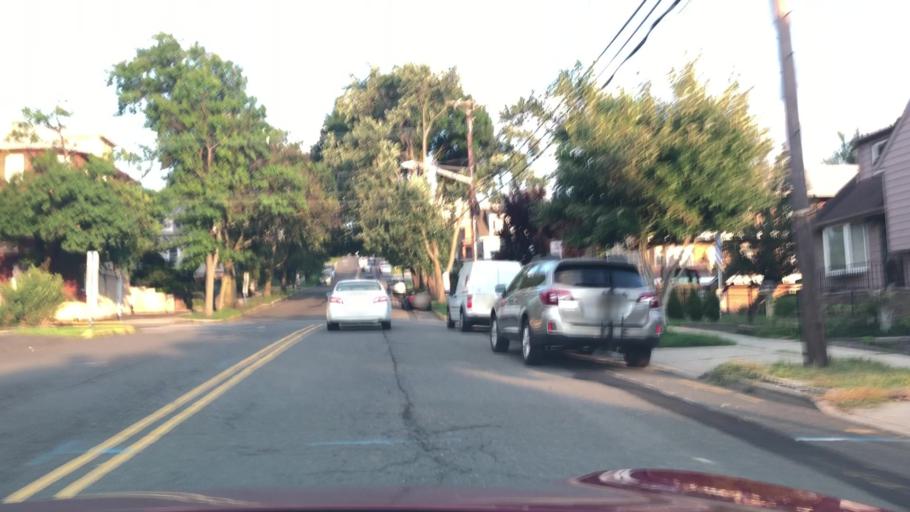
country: US
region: New Jersey
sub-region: Bergen County
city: Palisades Park
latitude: 40.8430
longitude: -73.9917
